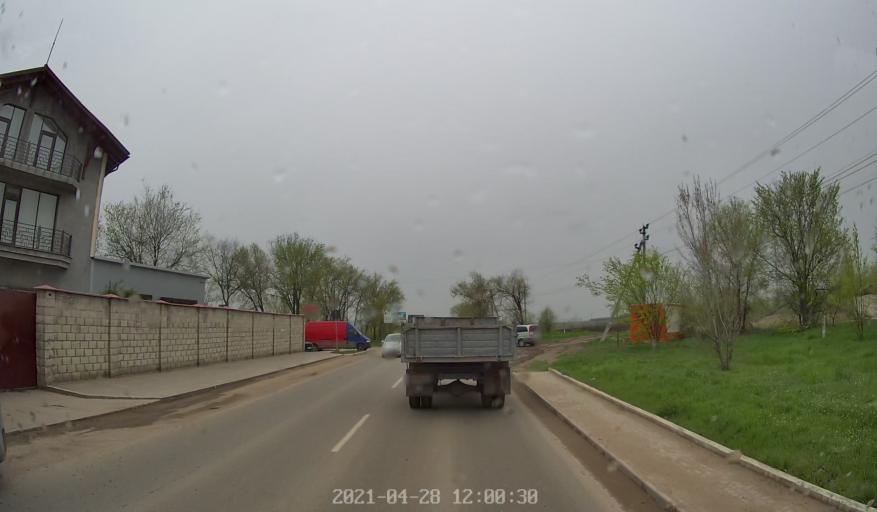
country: MD
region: Chisinau
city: Chisinau
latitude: 46.9860
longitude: 28.9292
